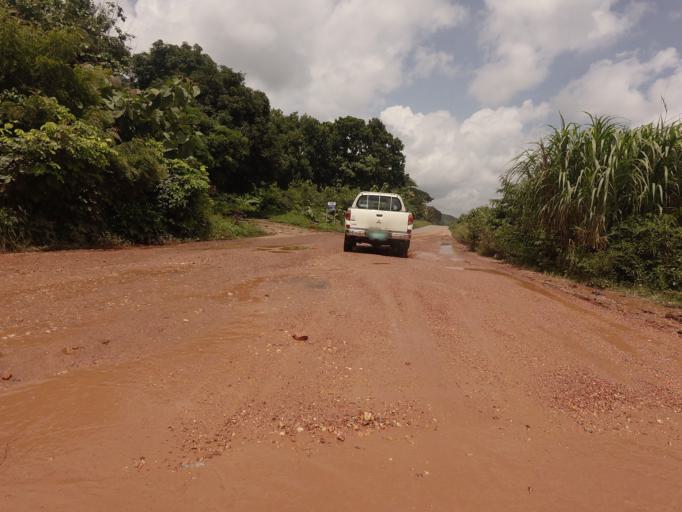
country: GH
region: Volta
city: Ho
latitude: 6.7346
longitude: 0.3474
